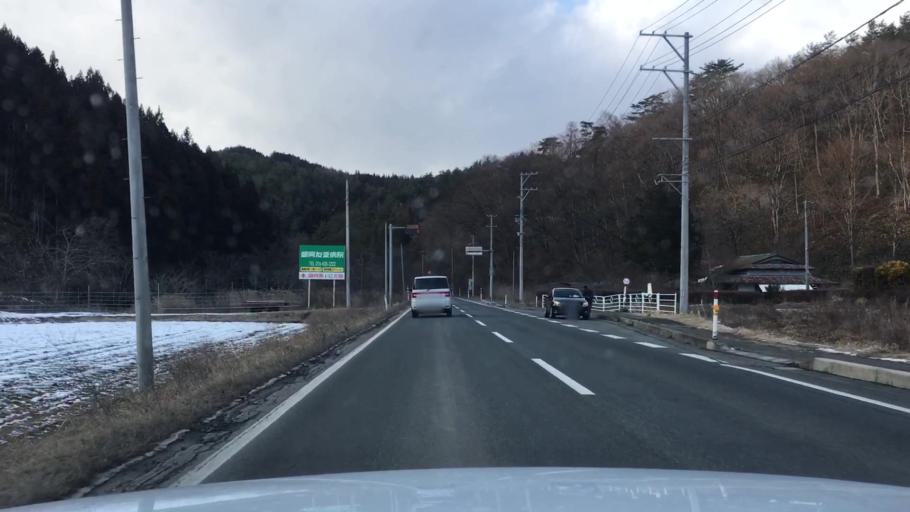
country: JP
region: Iwate
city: Morioka-shi
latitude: 39.6751
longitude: 141.2283
